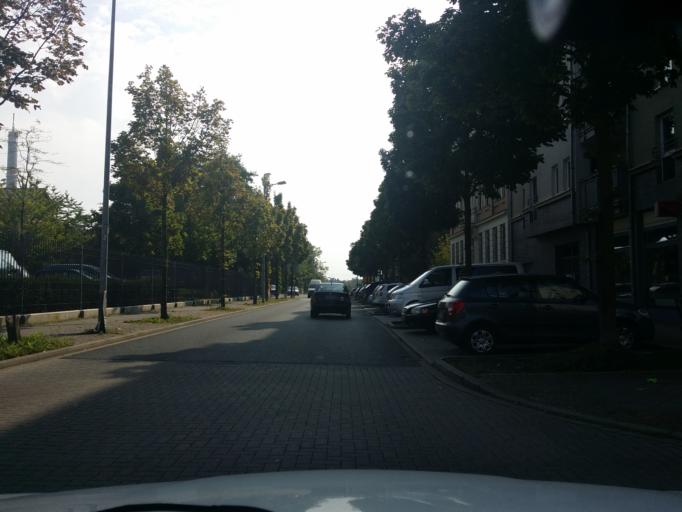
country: DE
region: Saxony
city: Leipzig
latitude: 51.3167
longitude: 12.3829
